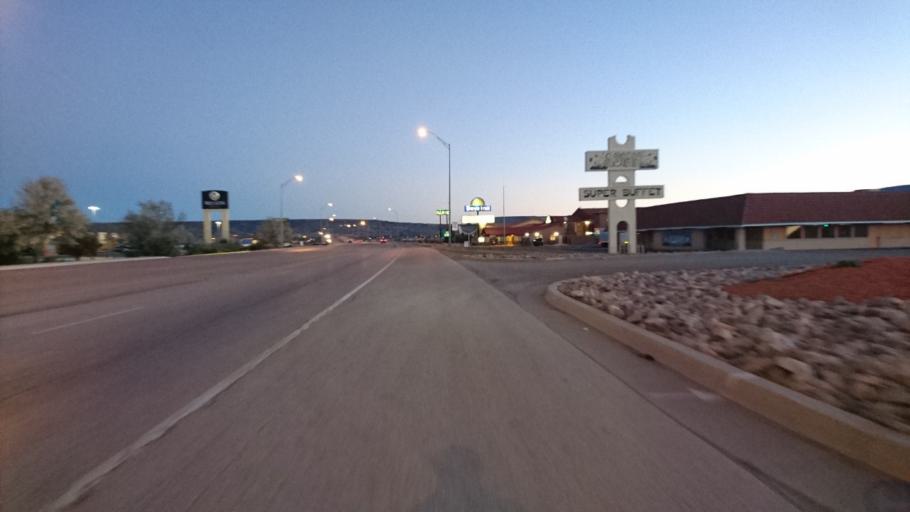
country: US
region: New Mexico
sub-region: Cibola County
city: Grants
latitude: 35.1296
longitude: -107.8272
